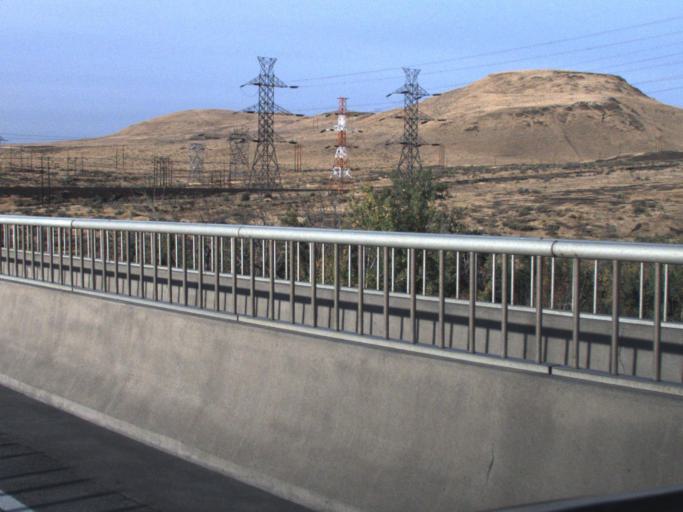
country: US
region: Oregon
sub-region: Umatilla County
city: Umatilla
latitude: 45.9346
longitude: -119.3300
